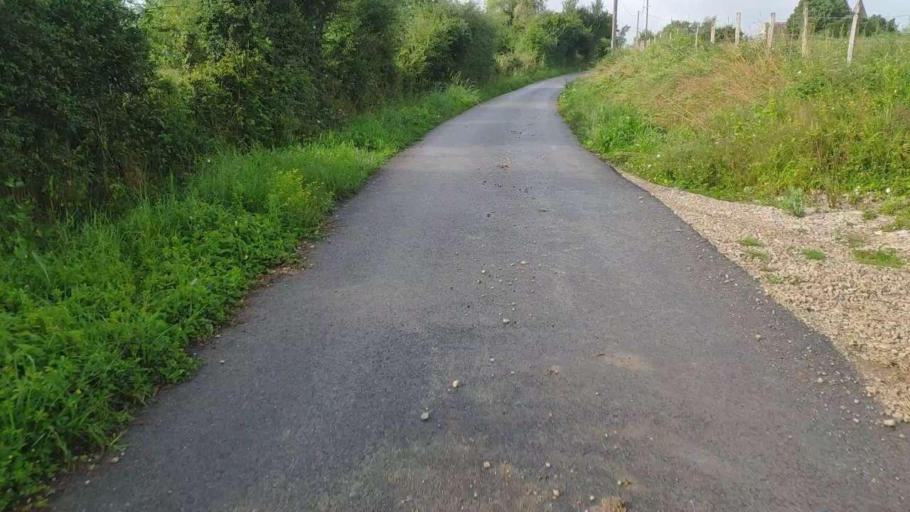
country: FR
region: Franche-Comte
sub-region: Departement du Jura
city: Mont-sous-Vaudrey
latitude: 46.8754
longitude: 5.5285
